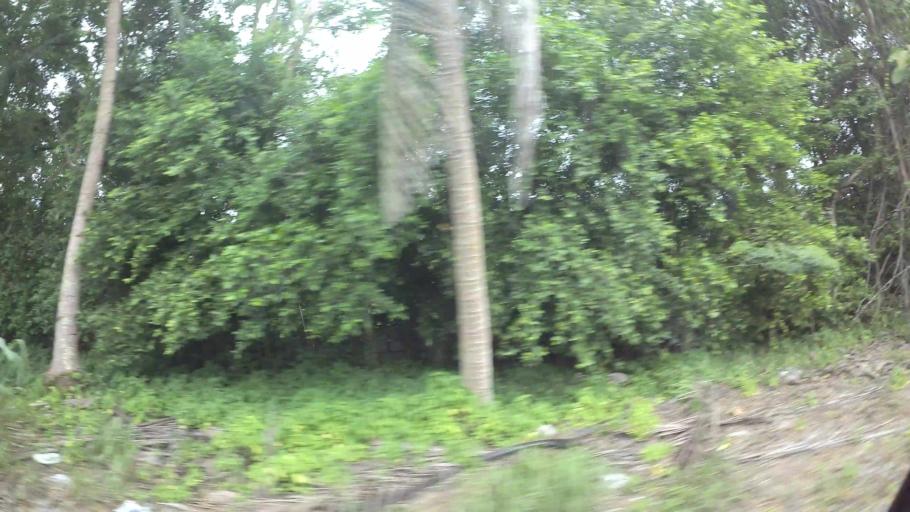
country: TH
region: Chon Buri
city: Si Racha
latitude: 13.1970
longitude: 100.9978
